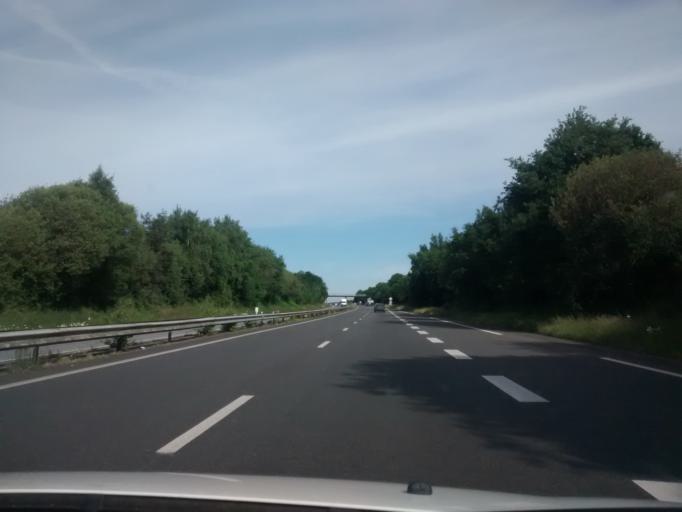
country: FR
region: Brittany
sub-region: Departement des Cotes-d'Armor
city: Caulnes
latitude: 48.2796
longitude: -2.1901
